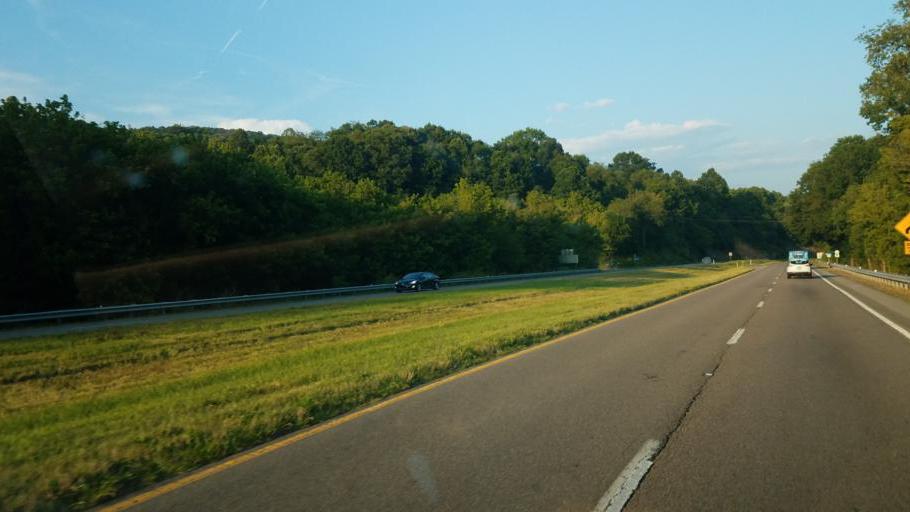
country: US
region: Virginia
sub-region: Scott County
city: Gate City
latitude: 36.6338
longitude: -82.6180
